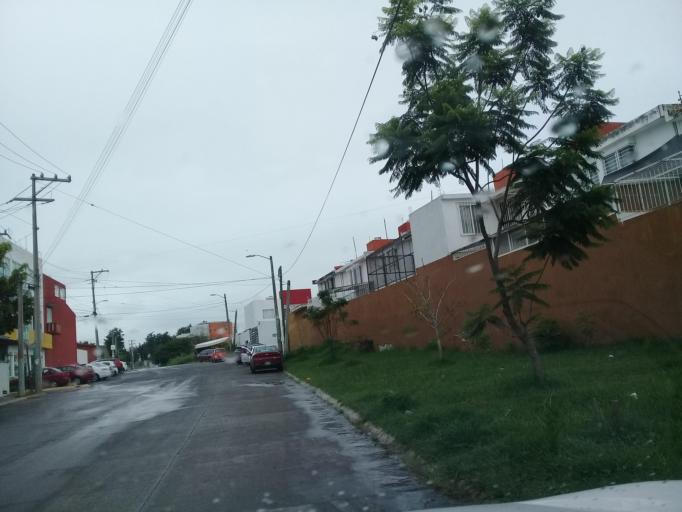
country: MX
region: Veracruz
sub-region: Emiliano Zapata
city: Jacarandas
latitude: 19.4987
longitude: -96.8509
